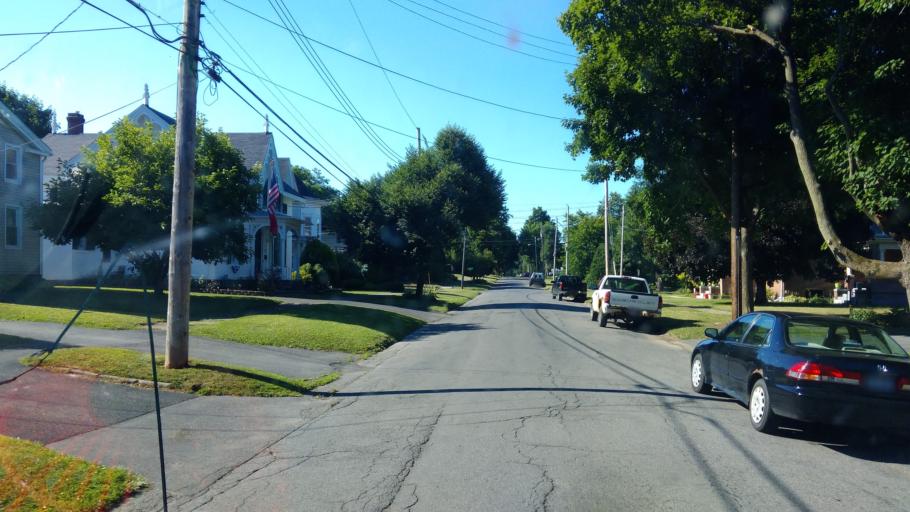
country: US
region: New York
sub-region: Wayne County
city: Lyons
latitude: 43.0665
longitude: -76.9875
